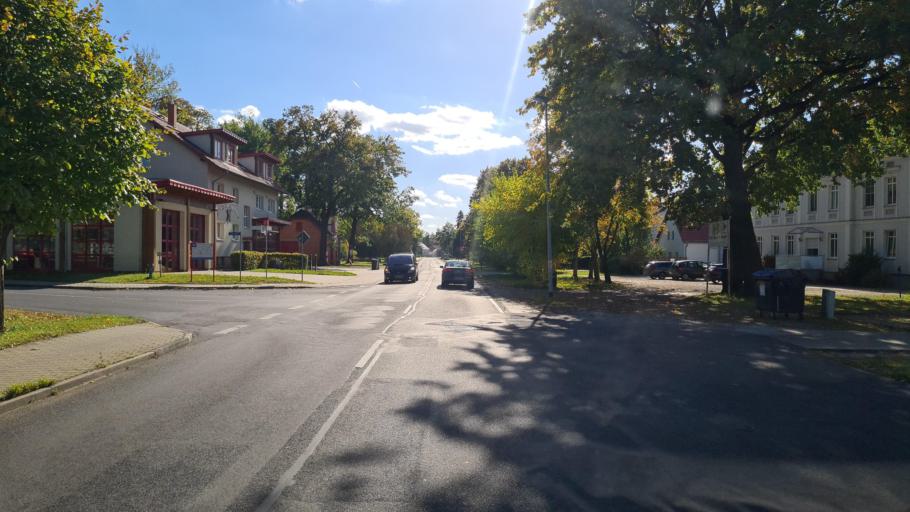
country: DE
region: Brandenburg
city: Kolkwitz
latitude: 51.7560
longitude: 14.2501
